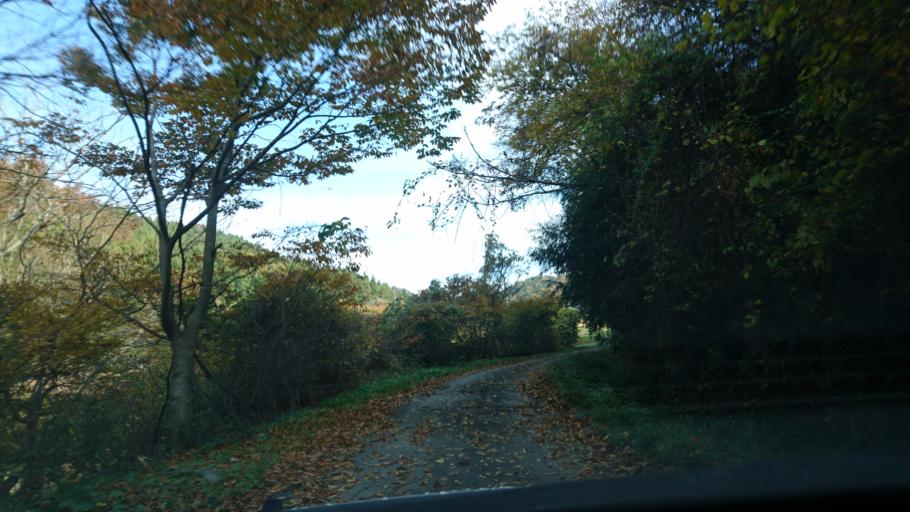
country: JP
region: Iwate
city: Ichinoseki
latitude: 38.9816
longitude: 141.1758
